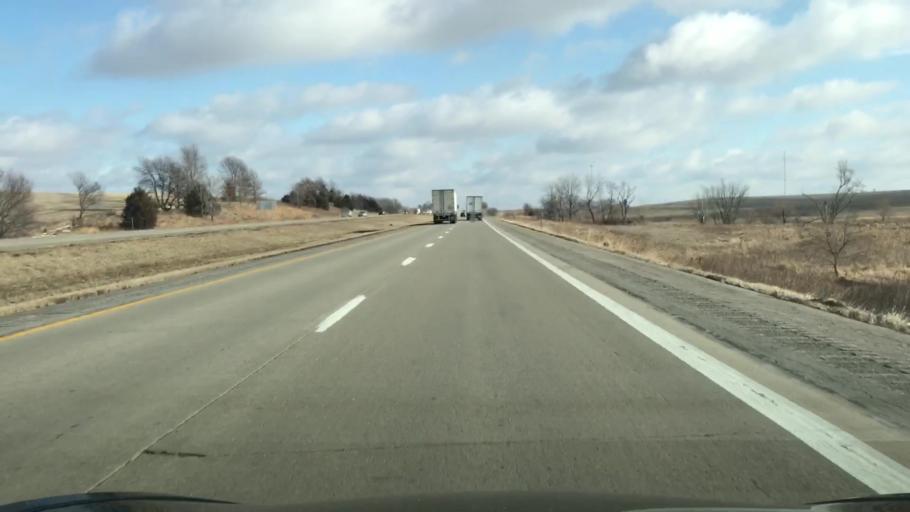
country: US
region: Iowa
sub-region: Cass County
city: Atlantic
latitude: 41.4972
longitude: -94.9875
